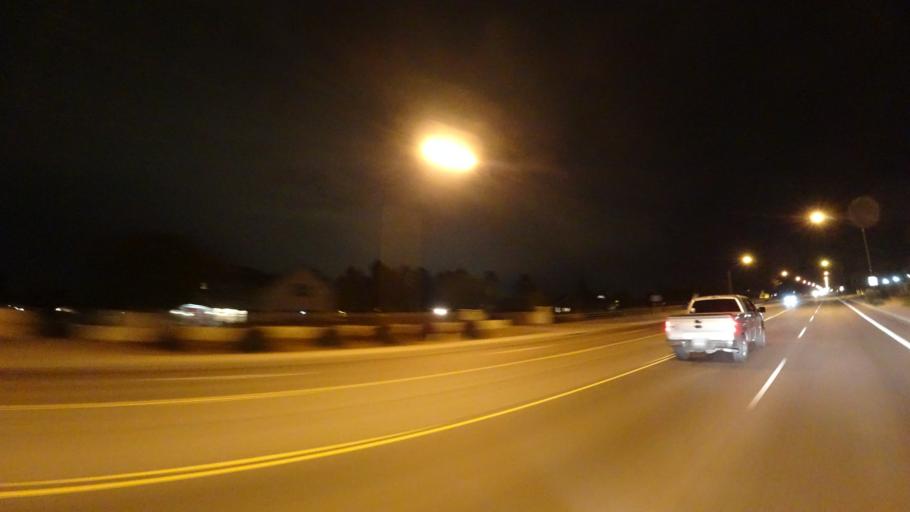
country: US
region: Arizona
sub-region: Maricopa County
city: Gilbert
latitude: 33.3521
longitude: -111.7384
